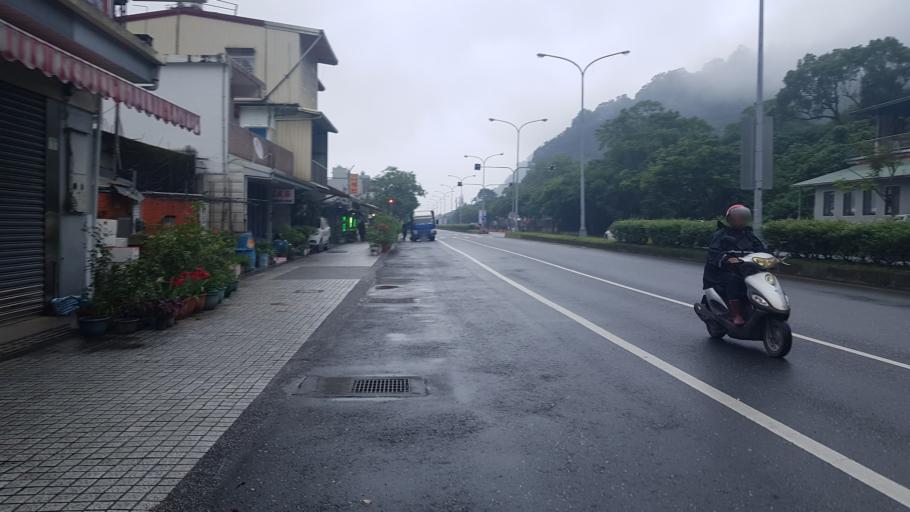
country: TW
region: Taiwan
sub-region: Hualien
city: Hualian
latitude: 24.1537
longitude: 121.6235
